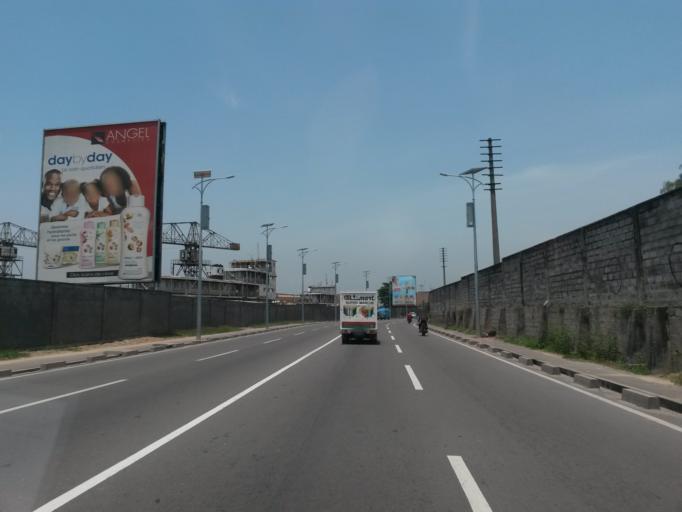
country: CD
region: Kinshasa
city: Kinshasa
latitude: -4.3042
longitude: 15.3245
